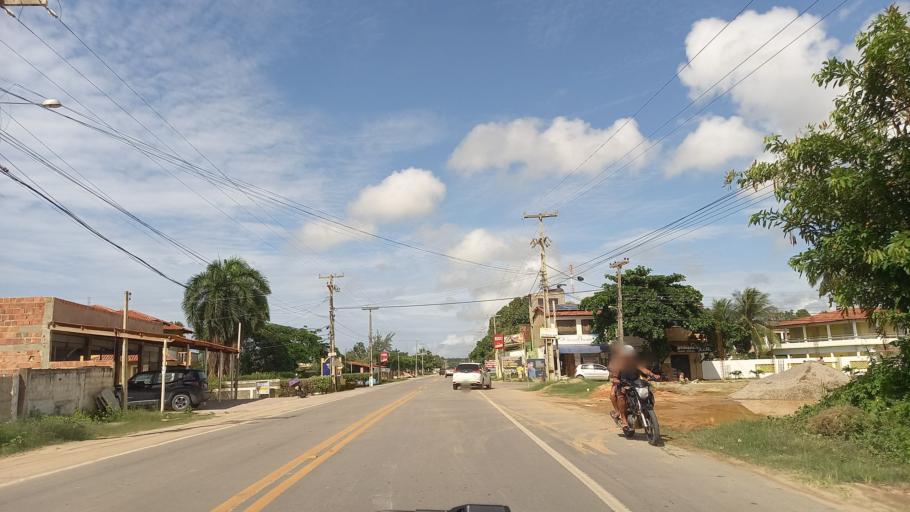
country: BR
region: Pernambuco
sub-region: Sao Jose Da Coroa Grande
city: Sao Jose da Coroa Grande
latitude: -8.9342
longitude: -35.1682
